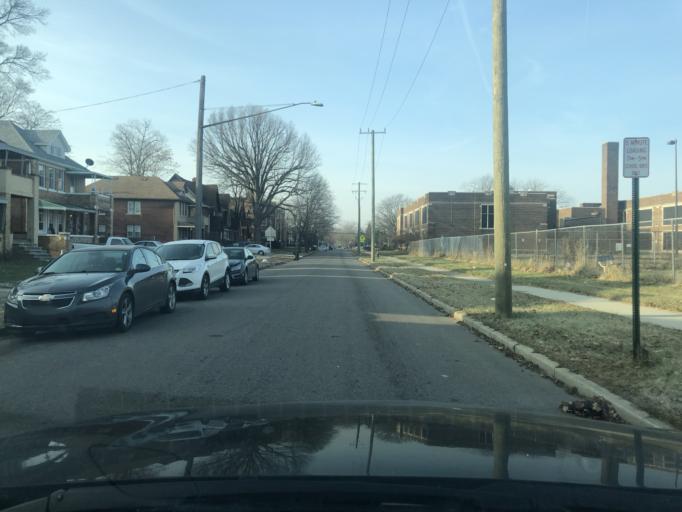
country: US
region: Michigan
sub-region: Wayne County
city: Highland Park
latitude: 42.3897
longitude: -83.1241
